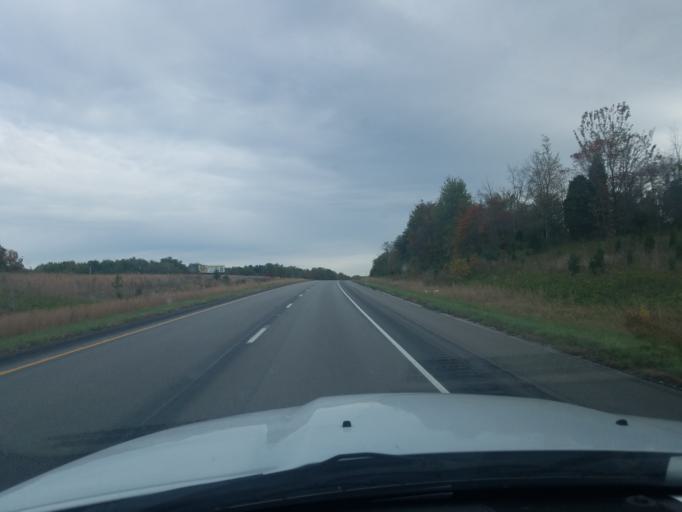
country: US
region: Indiana
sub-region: Spencer County
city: Dale
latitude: 38.2007
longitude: -87.1081
